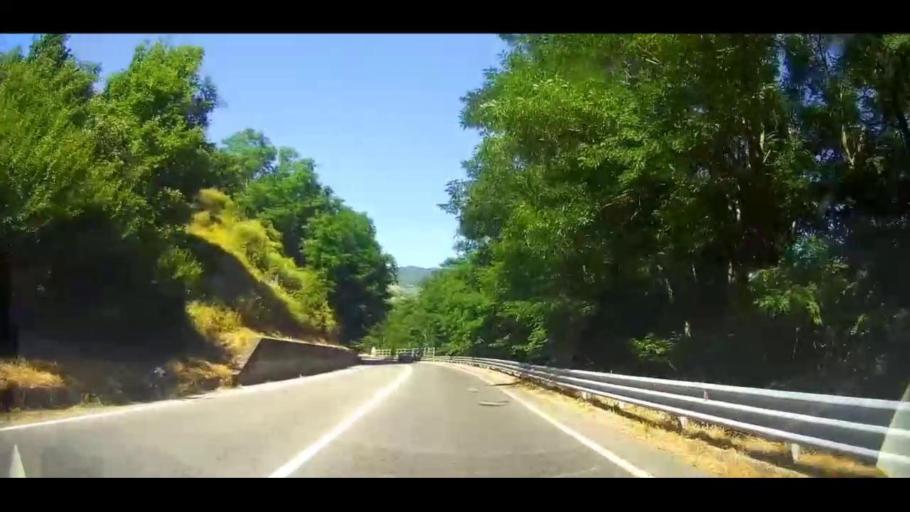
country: IT
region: Calabria
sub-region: Provincia di Cosenza
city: Rovito
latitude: 39.3112
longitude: 16.3279
